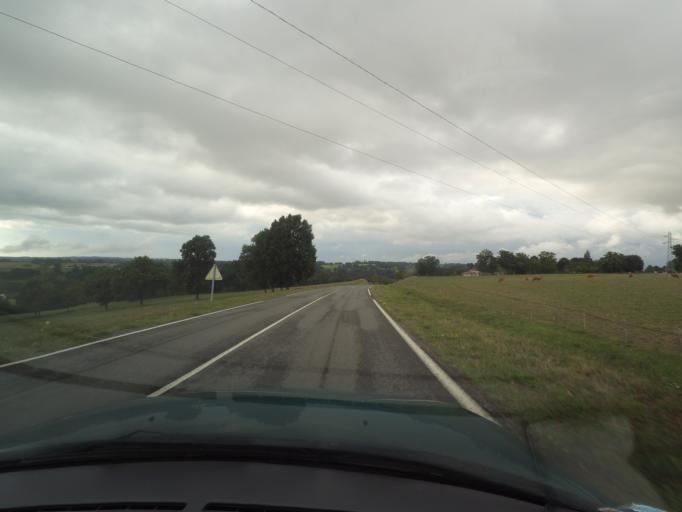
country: FR
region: Limousin
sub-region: Departement de la Haute-Vienne
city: Sereilhac
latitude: 45.7481
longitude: 1.1112
